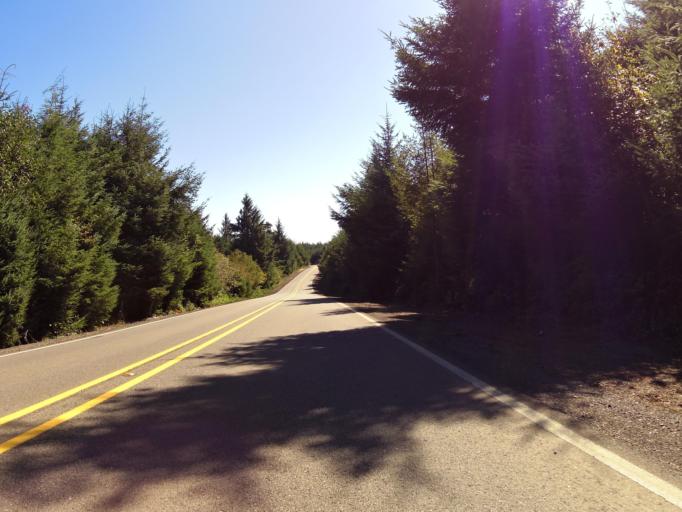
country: US
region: Oregon
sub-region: Coos County
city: Barview
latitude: 43.2731
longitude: -124.3552
